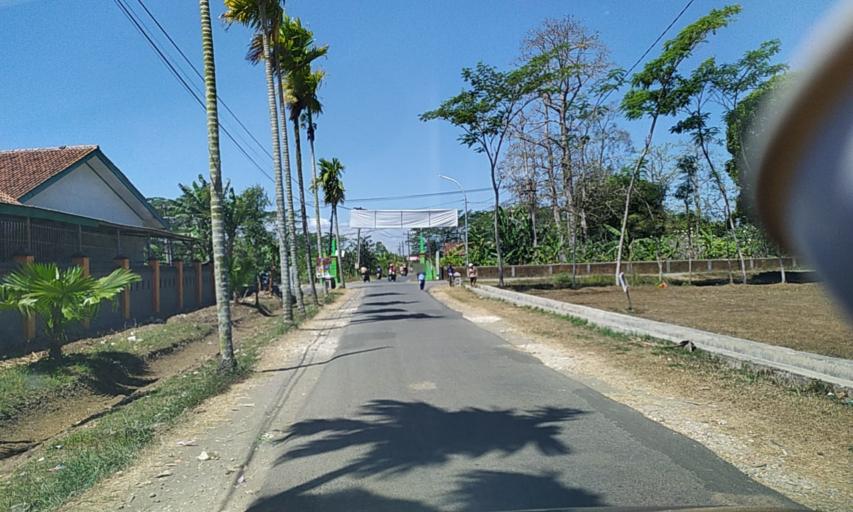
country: ID
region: Central Java
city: Adipala
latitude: -7.6609
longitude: 109.1145
